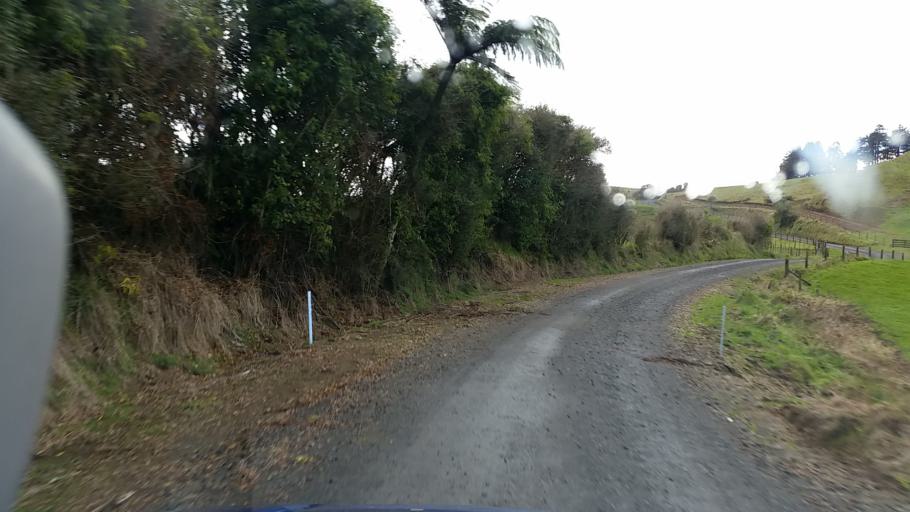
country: NZ
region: Taranaki
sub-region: South Taranaki District
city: Eltham
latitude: -39.2800
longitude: 174.3383
